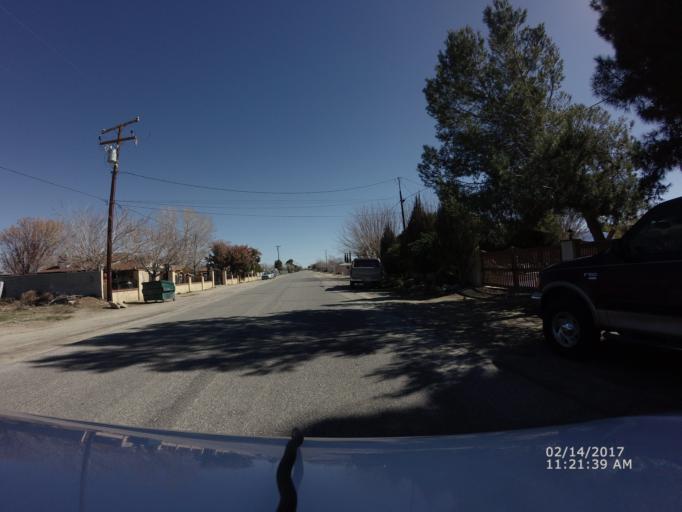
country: US
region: California
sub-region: Los Angeles County
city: Littlerock
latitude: 34.5596
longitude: -117.9685
